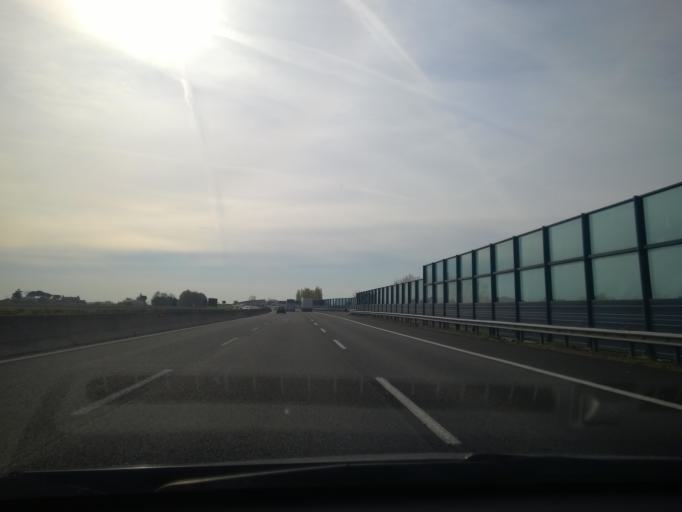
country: IT
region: Emilia-Romagna
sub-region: Forli-Cesena
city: Santa Maria Nuova
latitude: 44.2097
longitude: 12.1891
